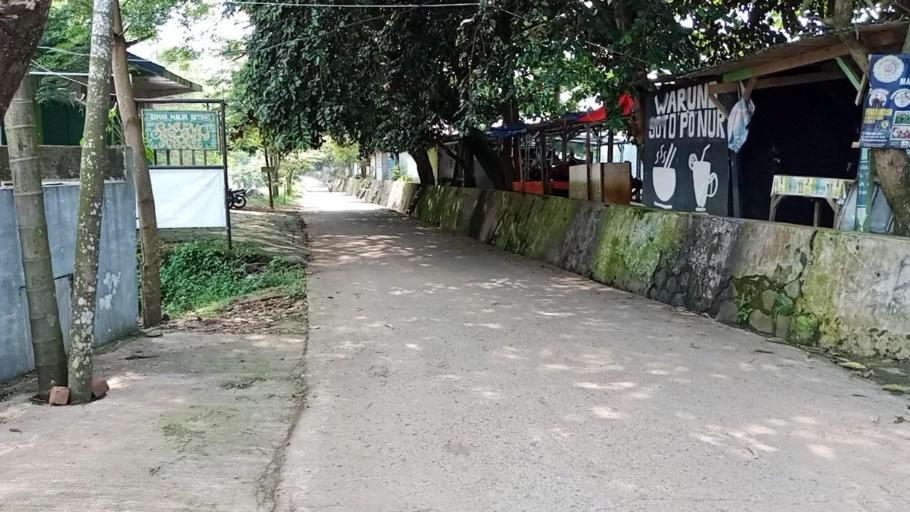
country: ID
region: West Java
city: Parung
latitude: -6.4209
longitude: 106.7476
